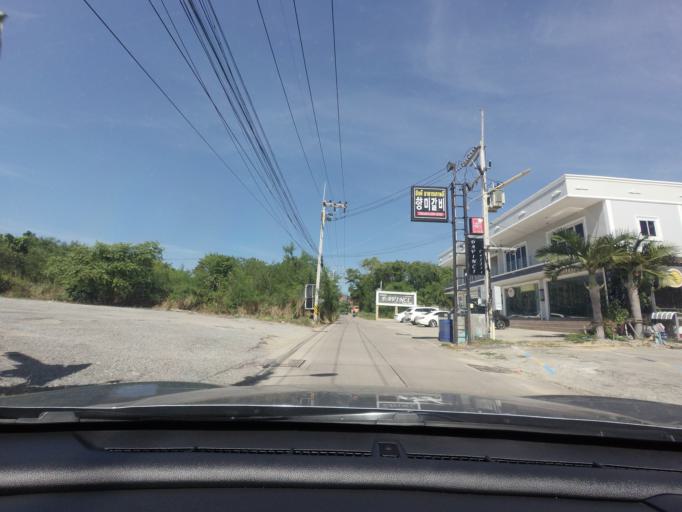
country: TH
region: Chon Buri
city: Phatthaya
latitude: 12.9462
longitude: 100.8983
